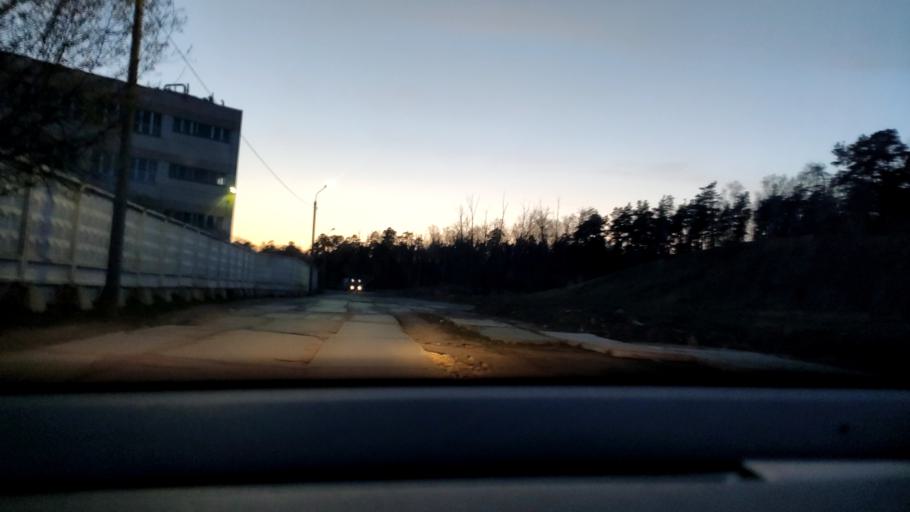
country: RU
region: Moscow
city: Rublevo
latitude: 55.7712
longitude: 37.3849
